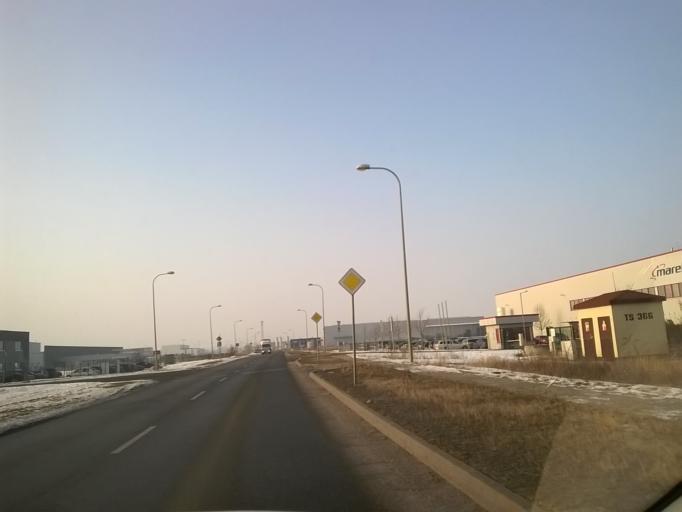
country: SK
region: Nitriansky
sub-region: Okres Nitra
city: Nitra
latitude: 48.3388
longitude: 18.0626
